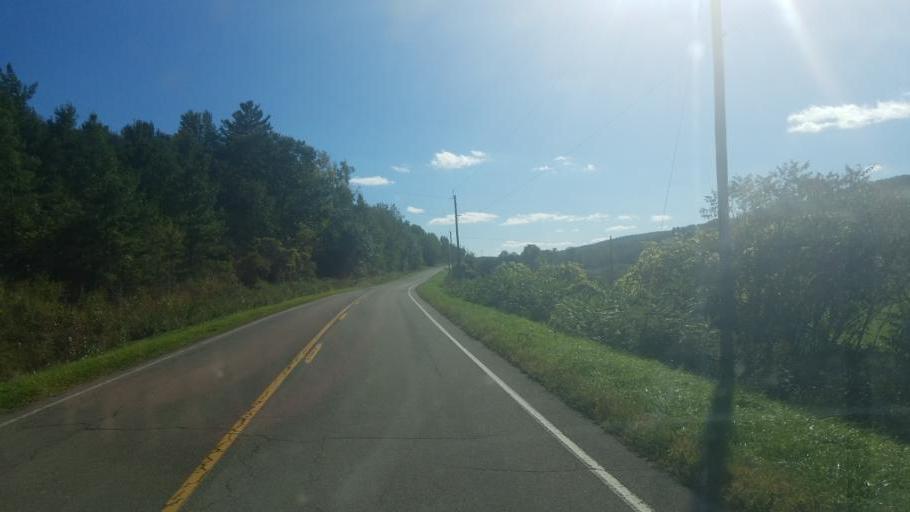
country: US
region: New York
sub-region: Allegany County
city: Friendship
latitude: 42.2897
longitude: -78.1191
